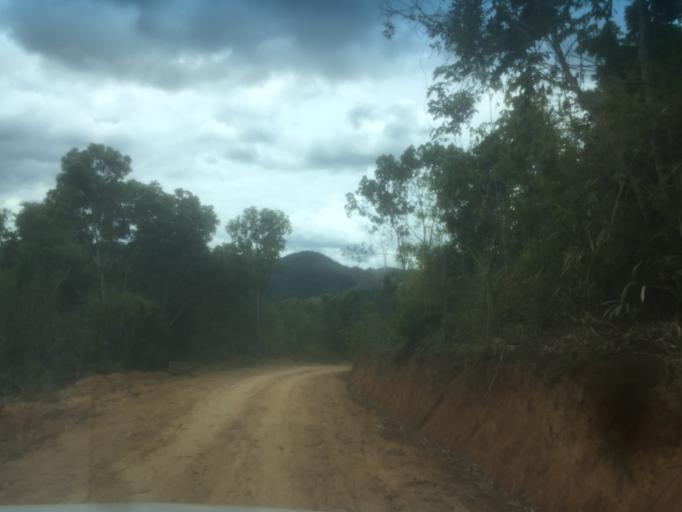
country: LA
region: Phongsali
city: Khoa
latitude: 20.9204
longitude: 102.5590
